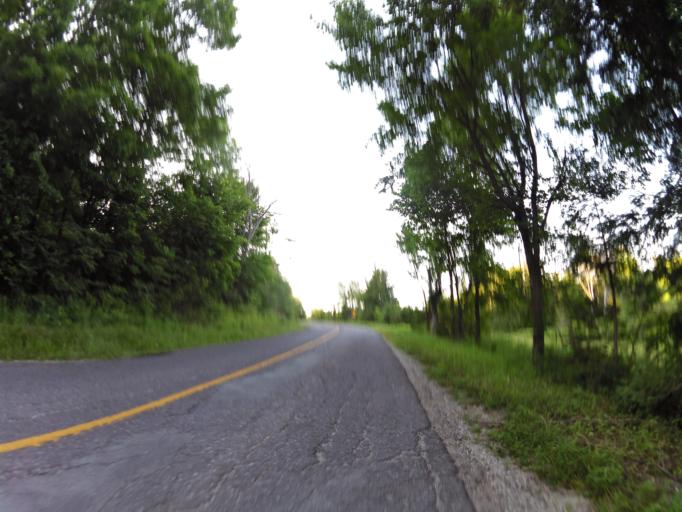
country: CA
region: Quebec
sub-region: Outaouais
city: Wakefield
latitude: 45.7146
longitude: -75.9606
